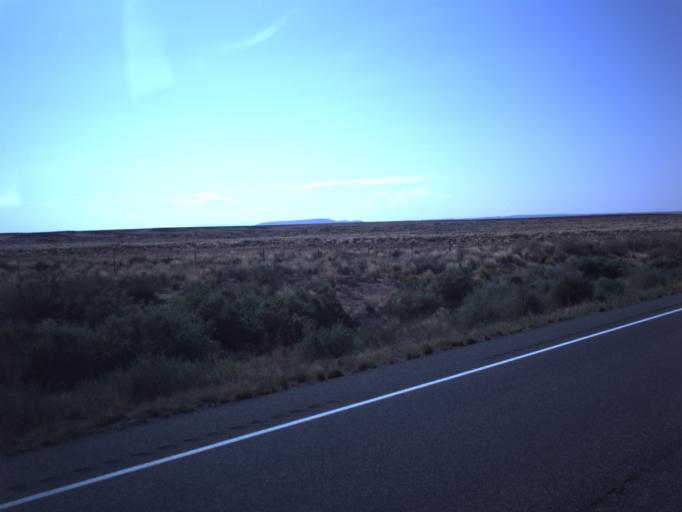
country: US
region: Utah
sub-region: San Juan County
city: Blanding
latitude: 37.3275
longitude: -109.5212
